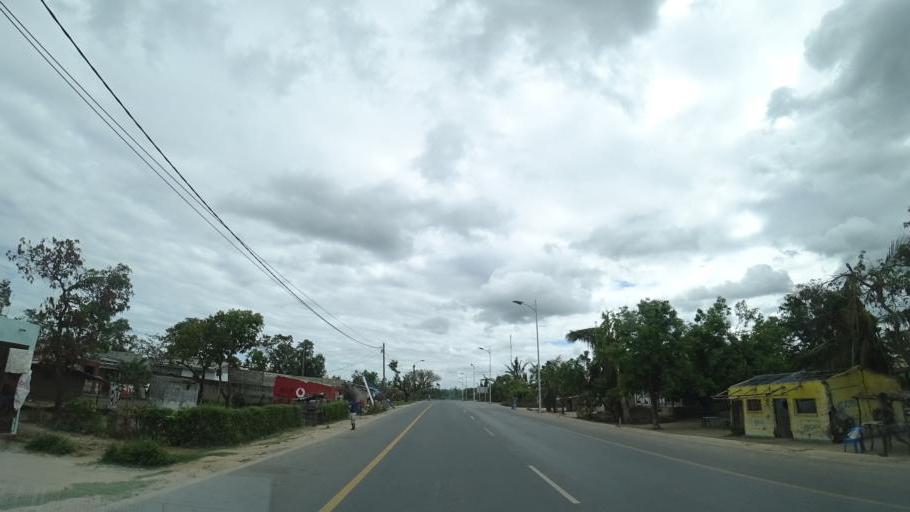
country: MZ
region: Sofala
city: Dondo
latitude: -19.5343
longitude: 34.6314
